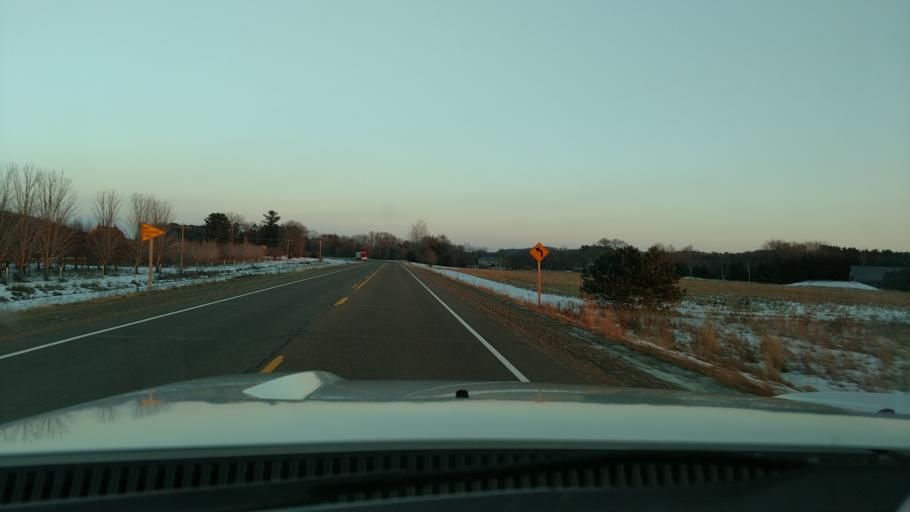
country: US
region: Wisconsin
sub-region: Pierce County
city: River Falls
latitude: 44.8982
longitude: -92.5925
